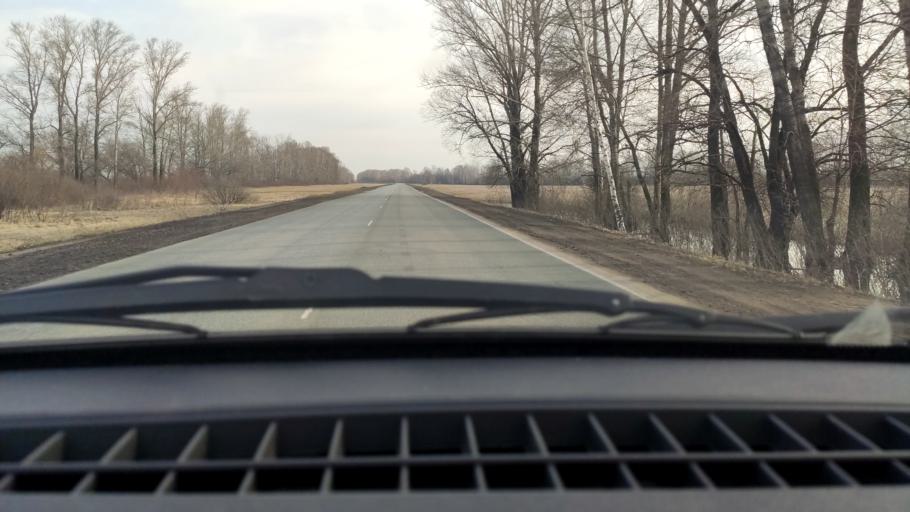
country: RU
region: Bashkortostan
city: Chishmy
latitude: 54.4034
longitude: 55.2151
